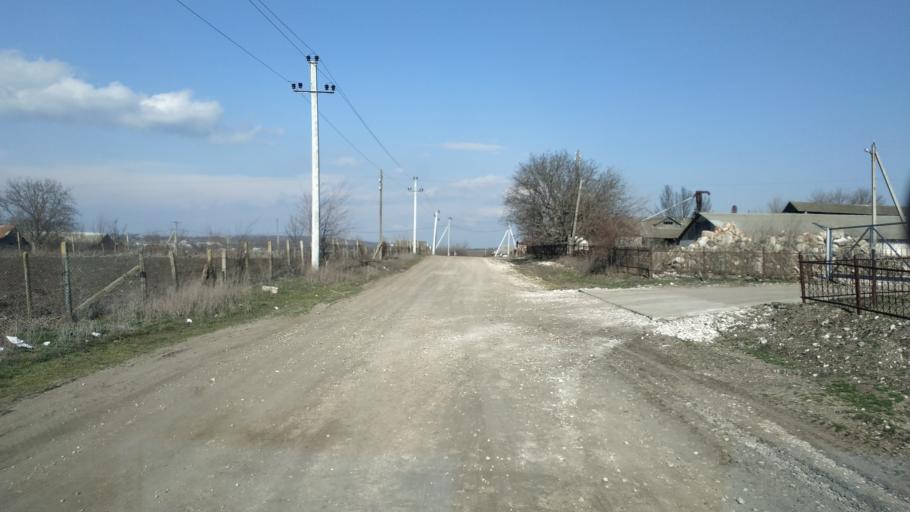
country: MD
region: Basarabeasca
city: Basarabeasca
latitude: 46.5743
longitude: 29.1223
